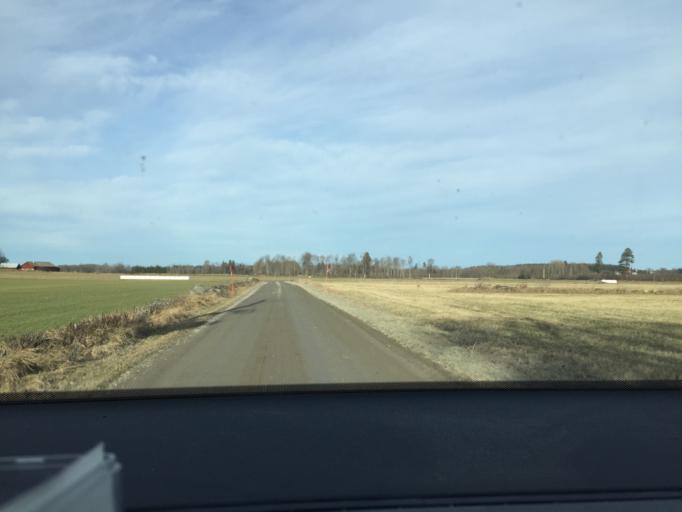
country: SE
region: OErebro
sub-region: Hallsbergs Kommun
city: Skollersta
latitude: 59.1338
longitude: 15.4287
